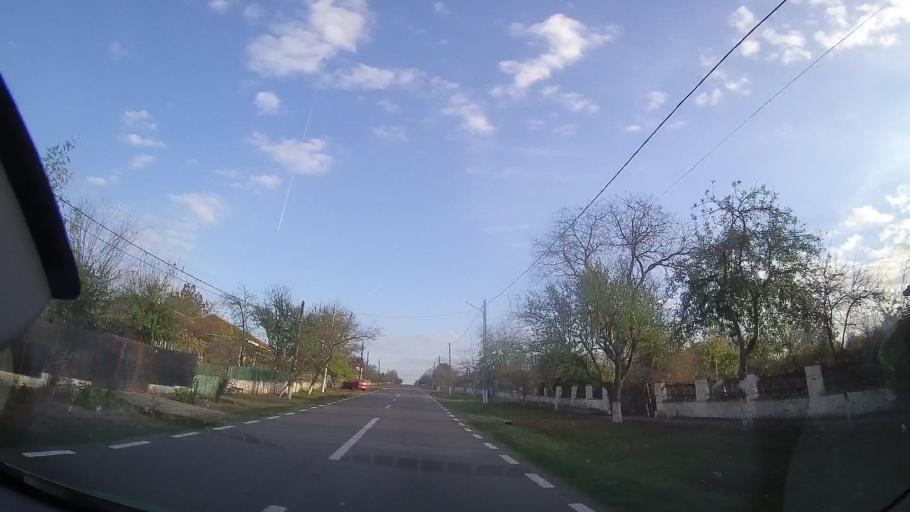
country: RO
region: Constanta
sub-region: Comuna Chirnogeni
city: Plopeni
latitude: 43.9610
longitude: 28.1431
